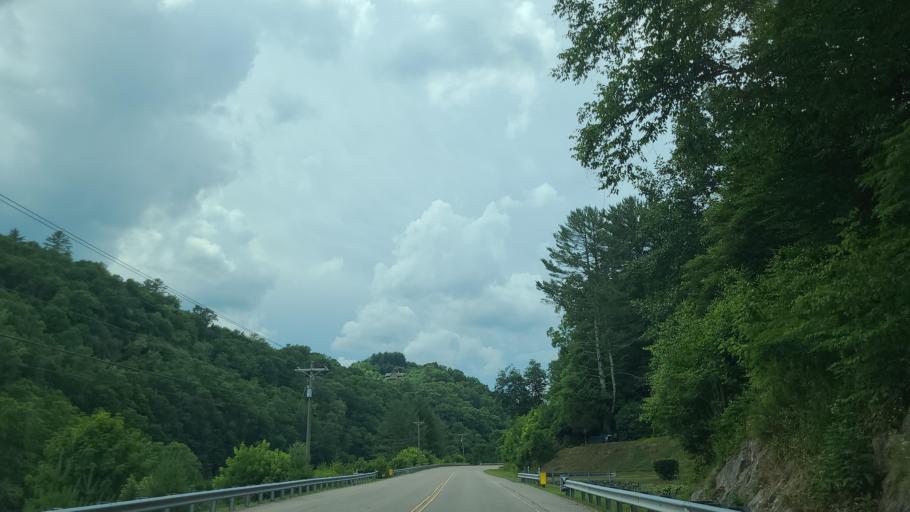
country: US
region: North Carolina
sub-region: Ashe County
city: Jefferson
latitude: 36.3785
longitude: -81.3989
